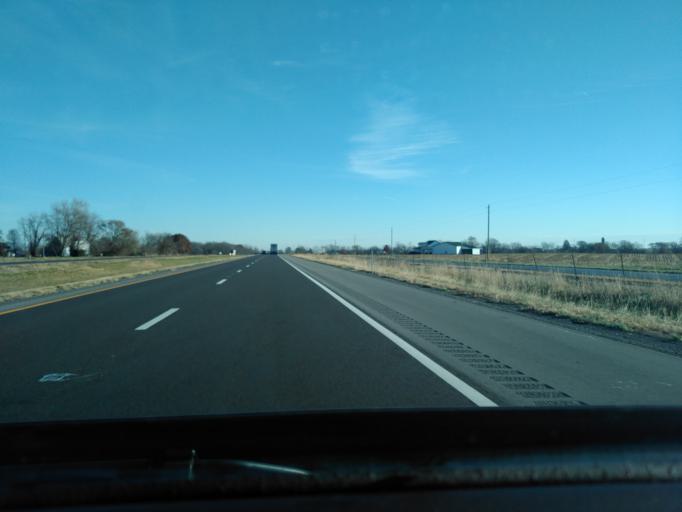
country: US
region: Illinois
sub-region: Madison County
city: Highland
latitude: 38.7959
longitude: -89.6093
